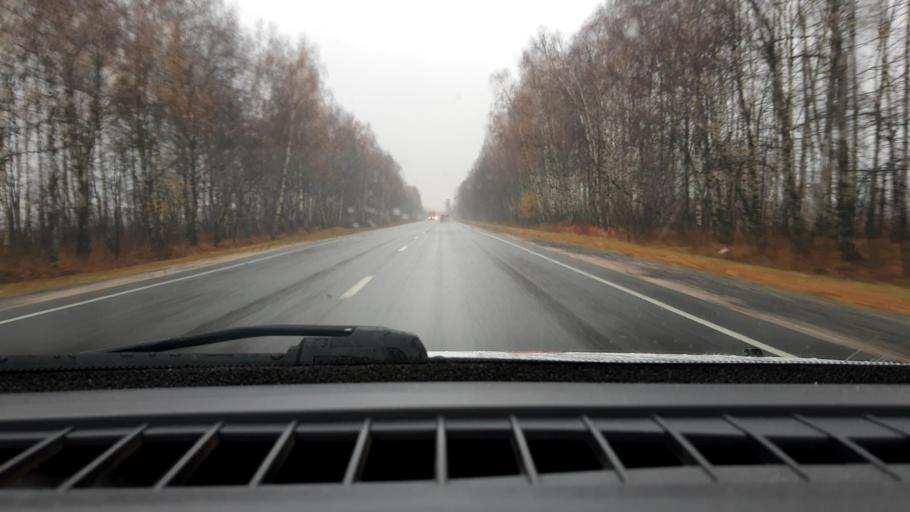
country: RU
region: Nizjnij Novgorod
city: Linda
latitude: 56.5514
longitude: 44.0216
